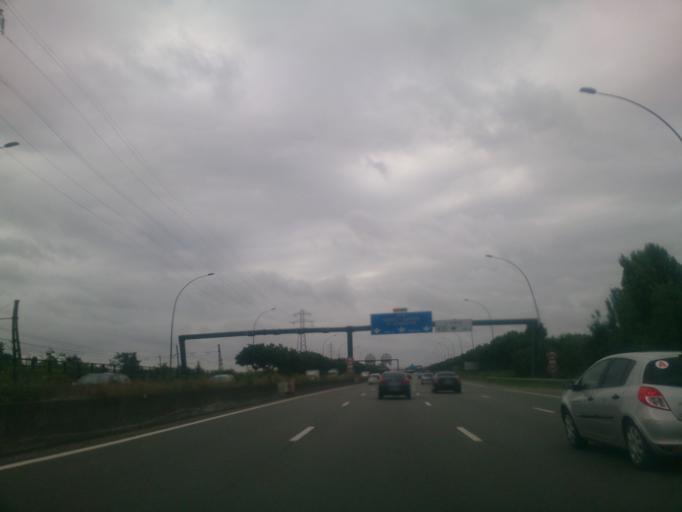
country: FR
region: Midi-Pyrenees
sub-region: Departement de la Haute-Garonne
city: Portet-sur-Garonne
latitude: 43.5623
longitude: 1.4175
